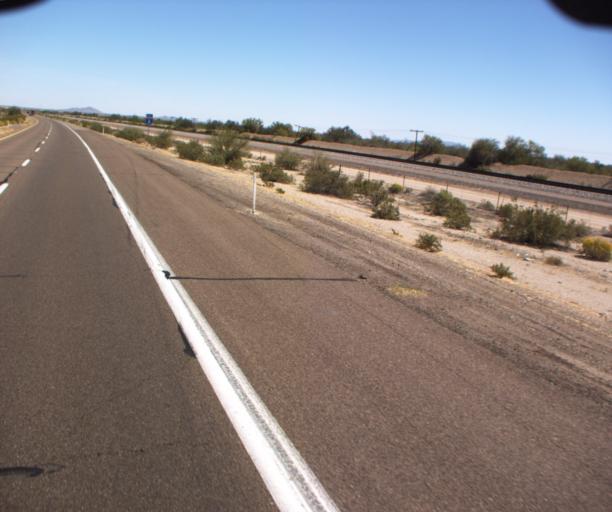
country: US
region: Arizona
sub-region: Yuma County
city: Wellton
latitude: 32.7319
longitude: -113.7107
